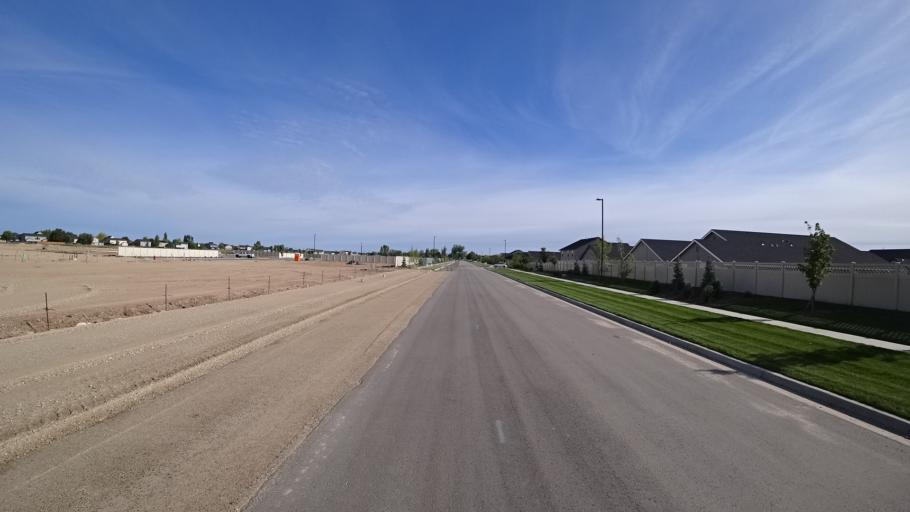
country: US
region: Idaho
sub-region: Ada County
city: Kuna
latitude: 43.5107
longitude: -116.4038
